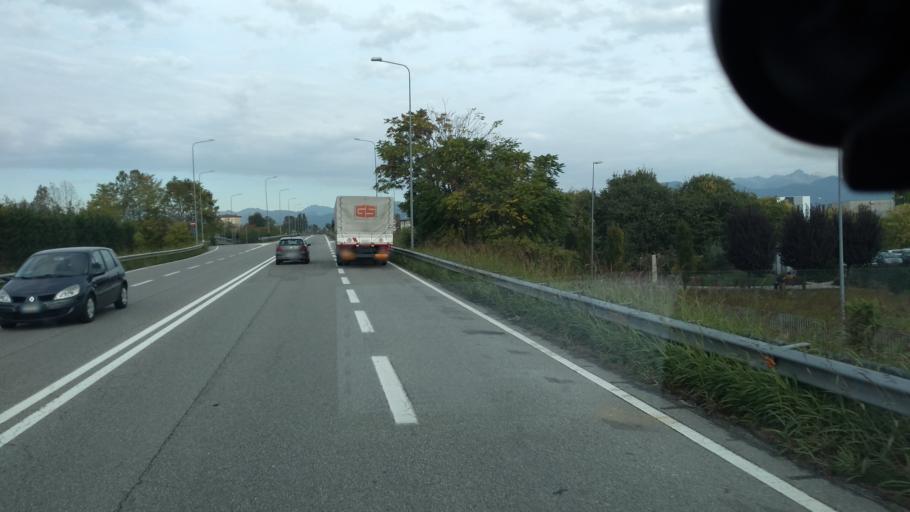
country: IT
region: Lombardy
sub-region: Provincia di Bergamo
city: Grassobbio
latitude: 45.6470
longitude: 9.7070
